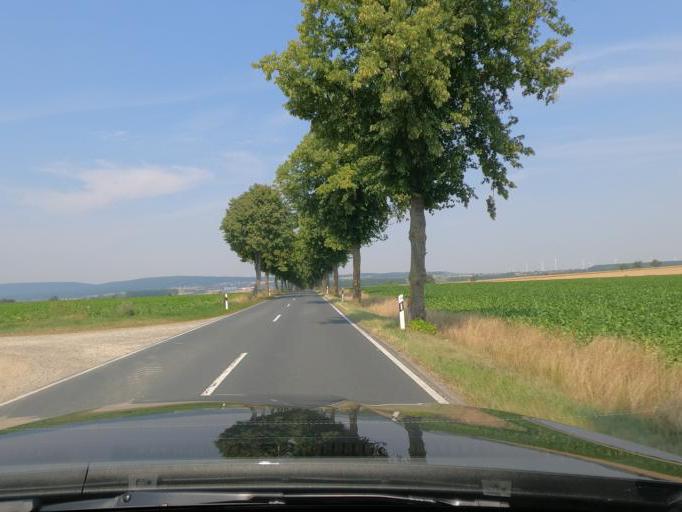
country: DE
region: Lower Saxony
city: Springe
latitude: 52.1785
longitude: 9.6400
